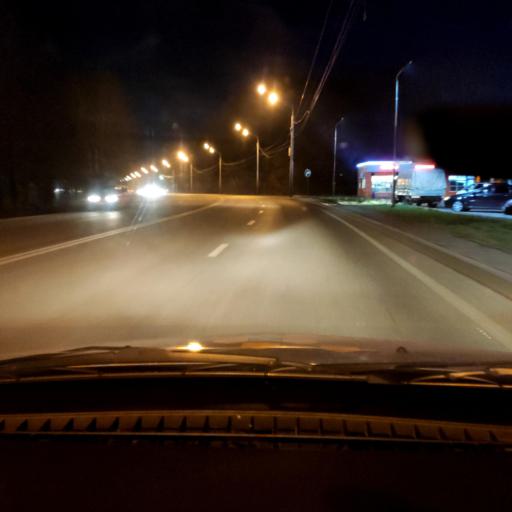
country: RU
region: Bashkortostan
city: Avdon
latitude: 54.6915
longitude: 55.8190
